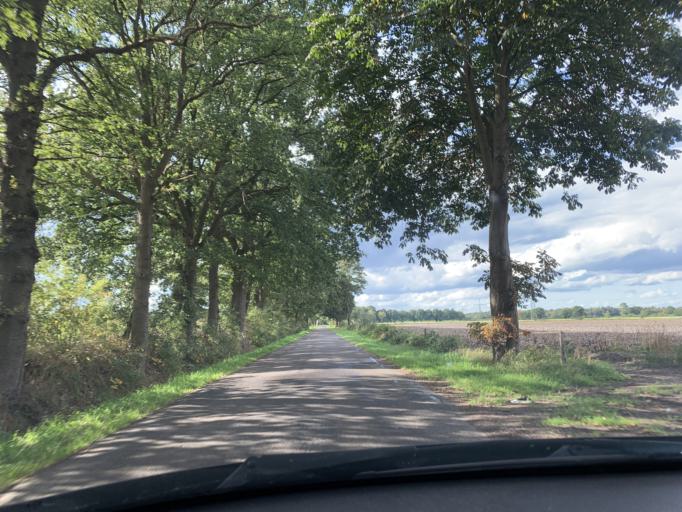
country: DE
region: Lower Saxony
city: Bockhorn
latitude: 53.3125
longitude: 8.0069
